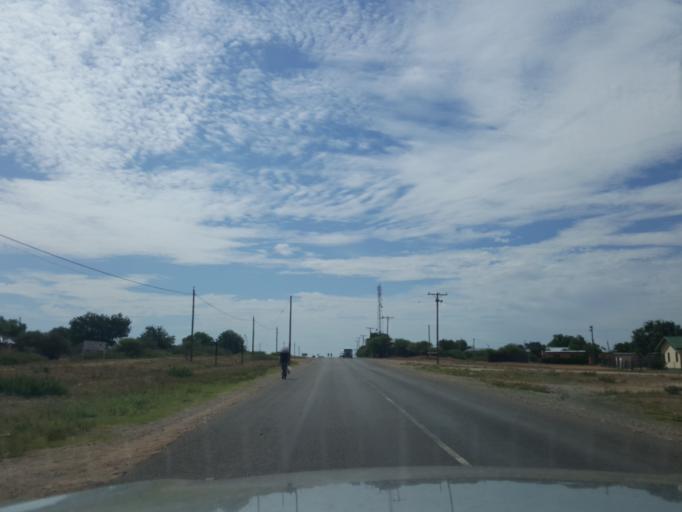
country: BW
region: Kweneng
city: Letlhakeng
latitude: -24.1060
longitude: 25.0325
